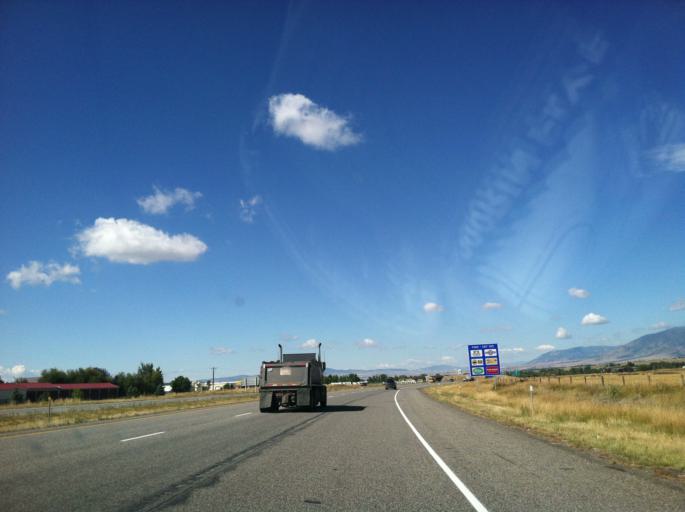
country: US
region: Montana
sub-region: Gallatin County
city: Bozeman
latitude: 45.7063
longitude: -111.0608
